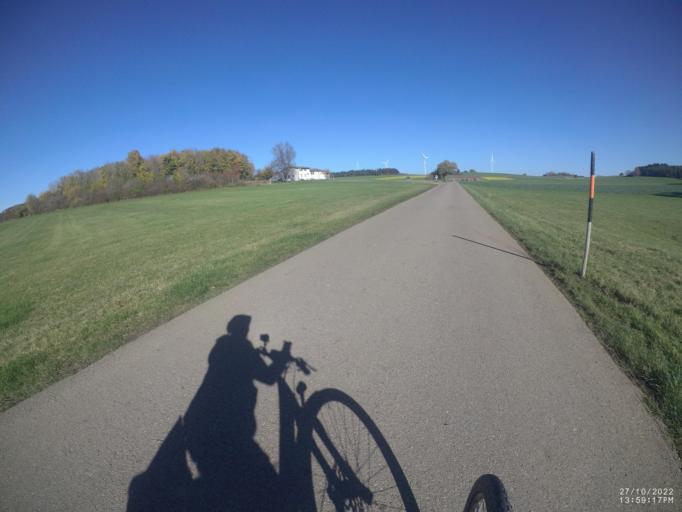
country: DE
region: Baden-Wuerttemberg
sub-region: Regierungsbezirk Stuttgart
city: Deggingen
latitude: 48.5672
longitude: 9.7311
